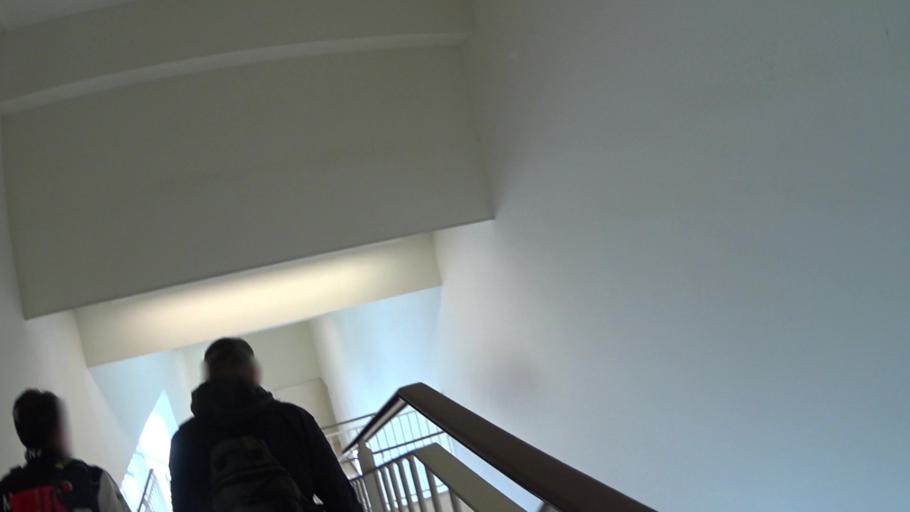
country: JP
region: Saitama
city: Yono
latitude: 35.8462
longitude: 139.6476
